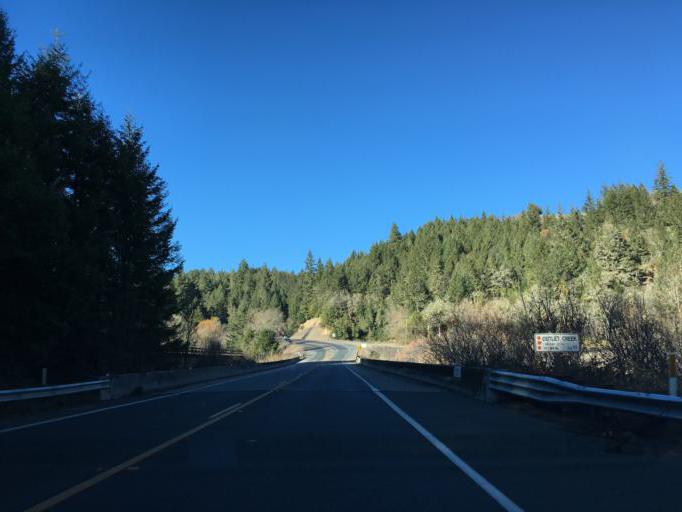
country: US
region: California
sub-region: Mendocino County
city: Brooktrails
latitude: 39.4622
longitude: -123.3502
